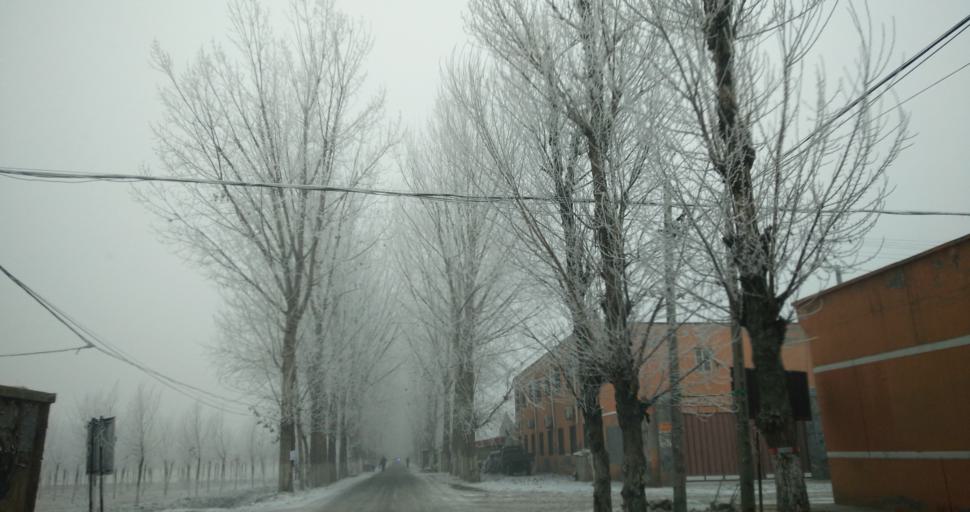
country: CN
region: Beijing
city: Yinghai
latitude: 39.7128
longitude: 116.4280
